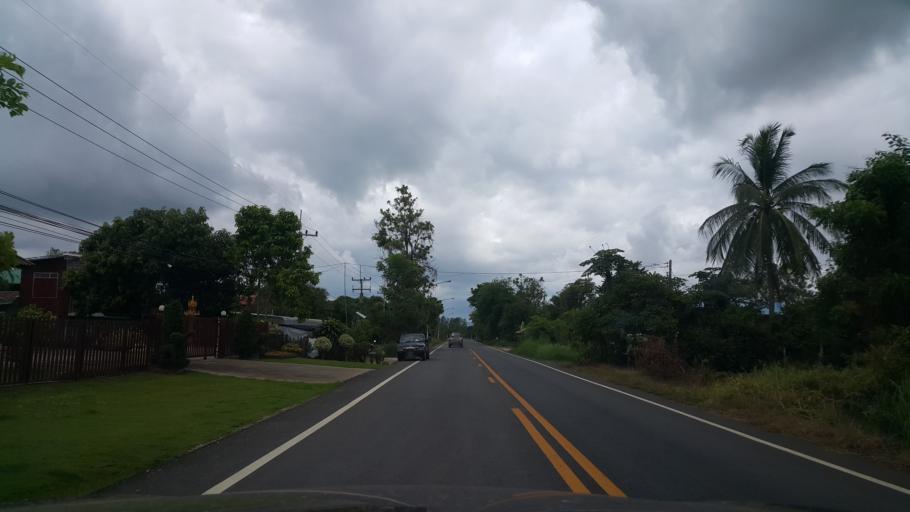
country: TH
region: Sukhothai
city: Sukhothai
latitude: 16.9154
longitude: 99.8659
